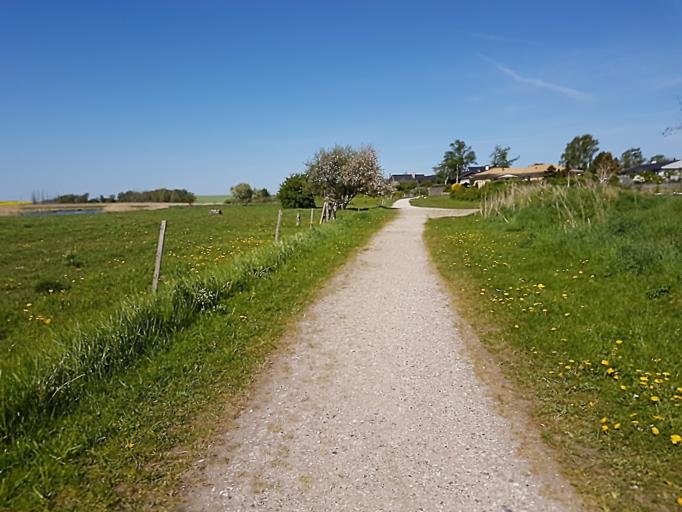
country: DK
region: Capital Region
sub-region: Egedal Kommune
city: Olstykke
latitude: 55.7926
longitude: 12.1351
